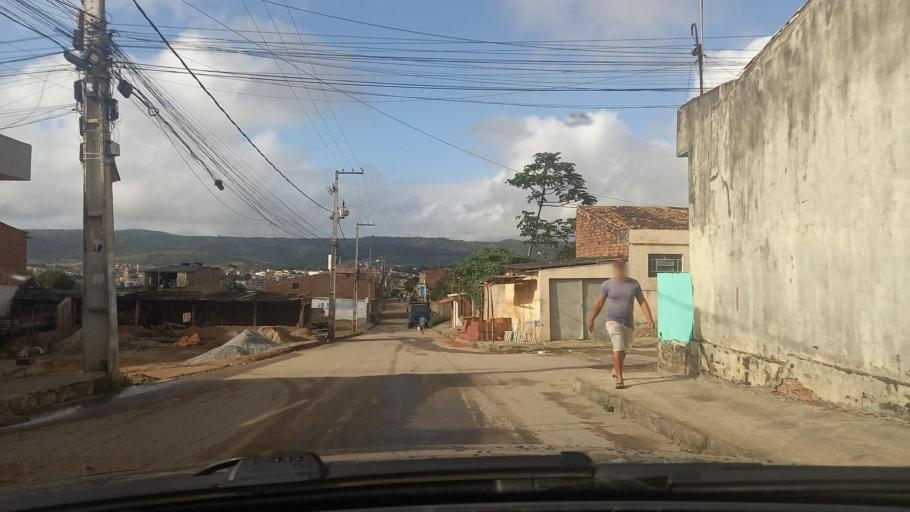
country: BR
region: Pernambuco
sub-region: Vitoria De Santo Antao
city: Vitoria de Santo Antao
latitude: -8.1119
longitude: -35.3080
